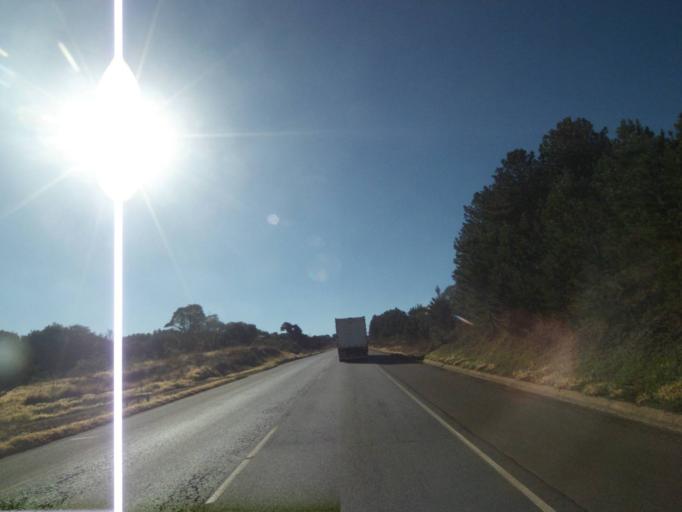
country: BR
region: Parana
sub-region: Tibagi
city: Tibagi
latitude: -24.5339
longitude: -50.4474
